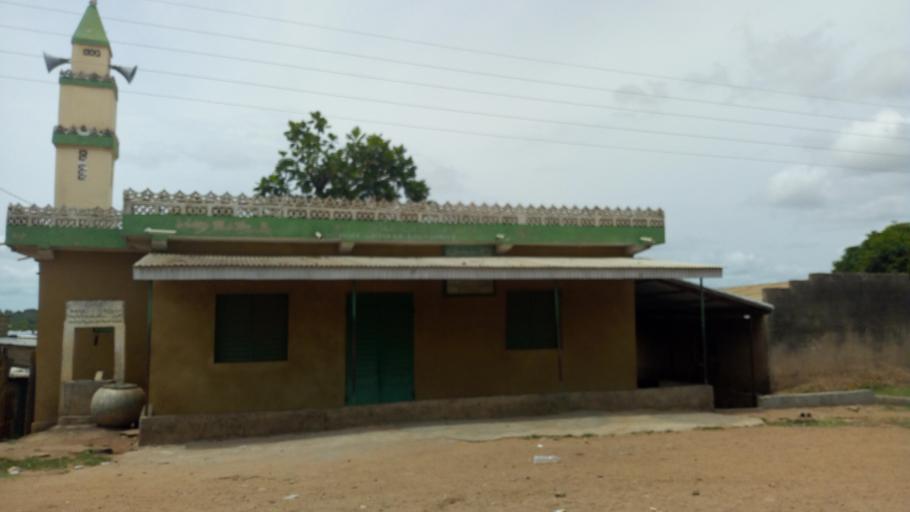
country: CI
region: Vallee du Bandama
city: Bouake
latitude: 7.7151
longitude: -5.0241
